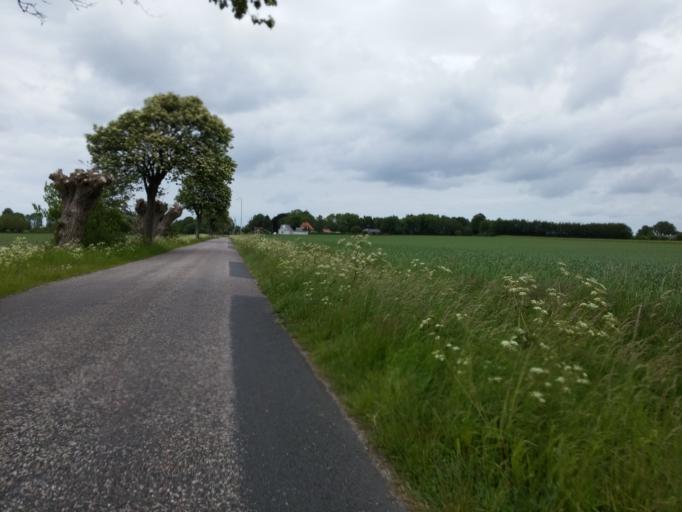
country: DK
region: South Denmark
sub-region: Kerteminde Kommune
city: Munkebo
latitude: 55.4448
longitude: 10.5206
